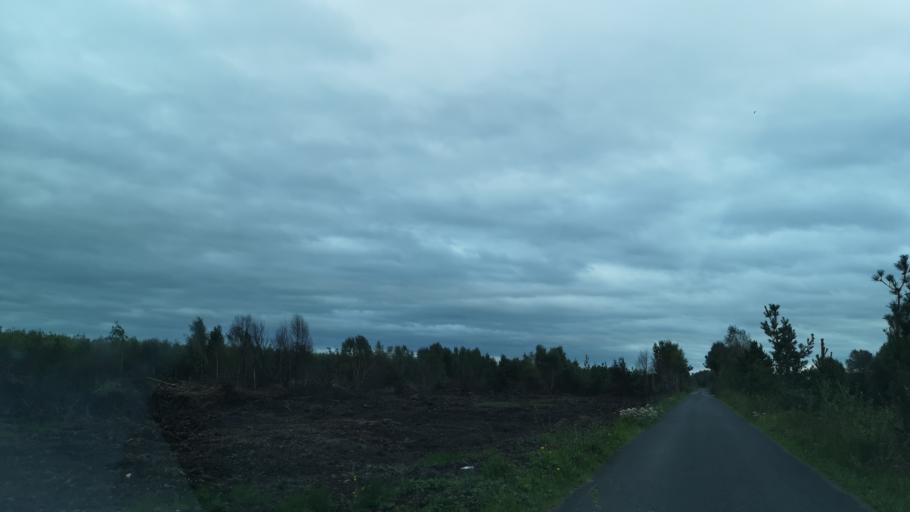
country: IE
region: Leinster
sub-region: Uibh Fhaili
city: Ferbane
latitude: 53.2077
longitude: -7.7237
